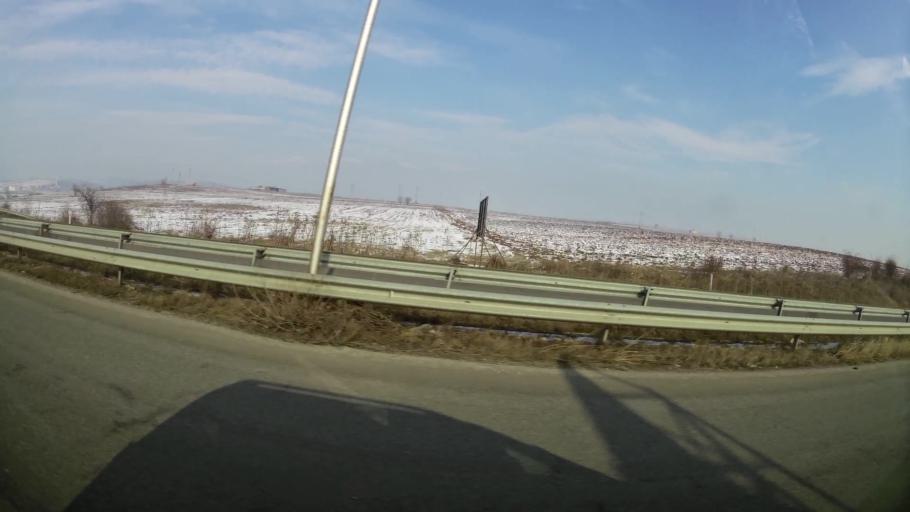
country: MK
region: Butel
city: Butel
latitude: 42.0346
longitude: 21.4711
